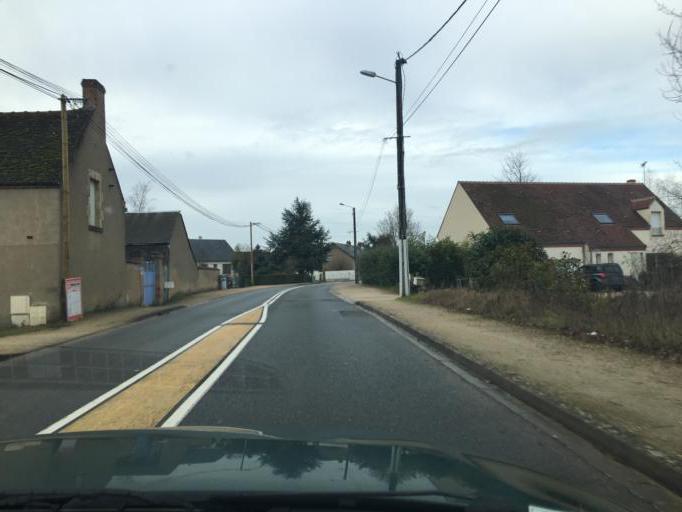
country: FR
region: Centre
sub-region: Departement du Loiret
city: Olivet
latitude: 47.8548
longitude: 1.8925
